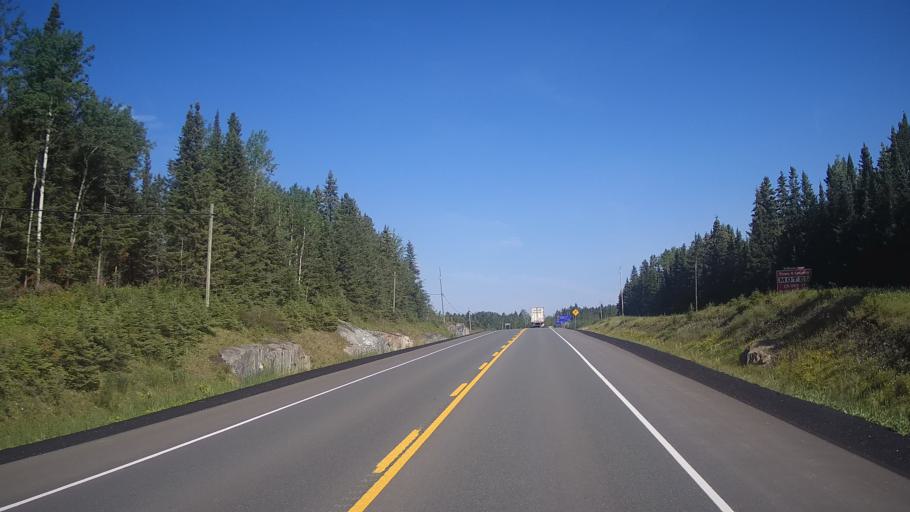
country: CA
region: Ontario
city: Dryden
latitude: 49.6671
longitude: -92.4887
